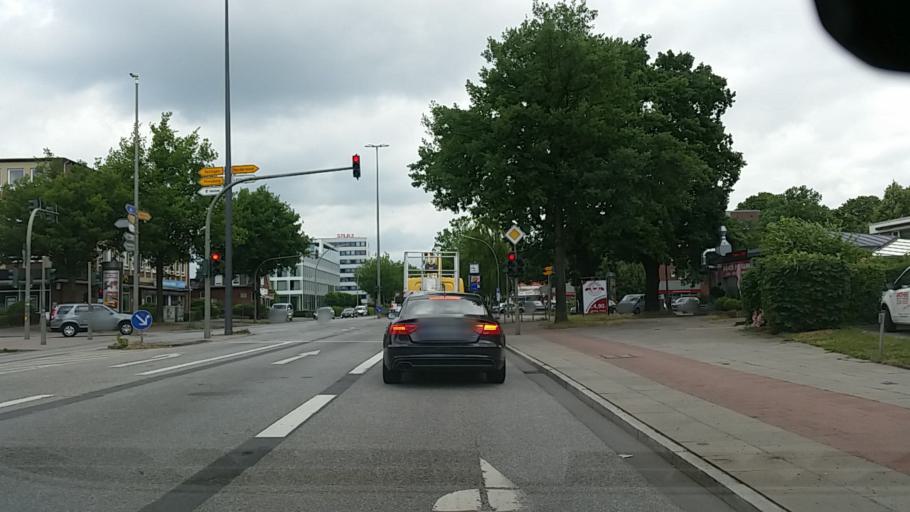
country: DE
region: Hamburg
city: Eidelstedt
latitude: 53.6324
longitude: 9.9109
